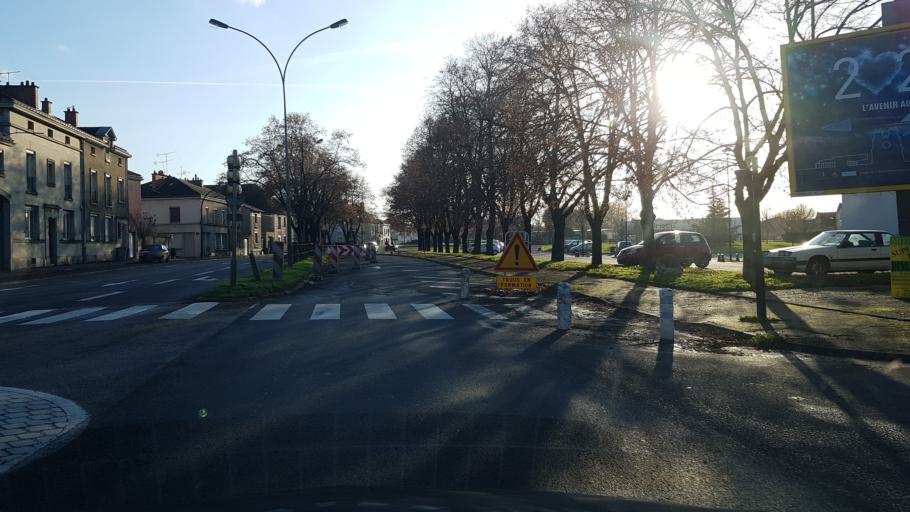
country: FR
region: Champagne-Ardenne
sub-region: Departement de la Marne
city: Vitry-le-Francois
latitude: 48.7287
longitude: 4.5819
